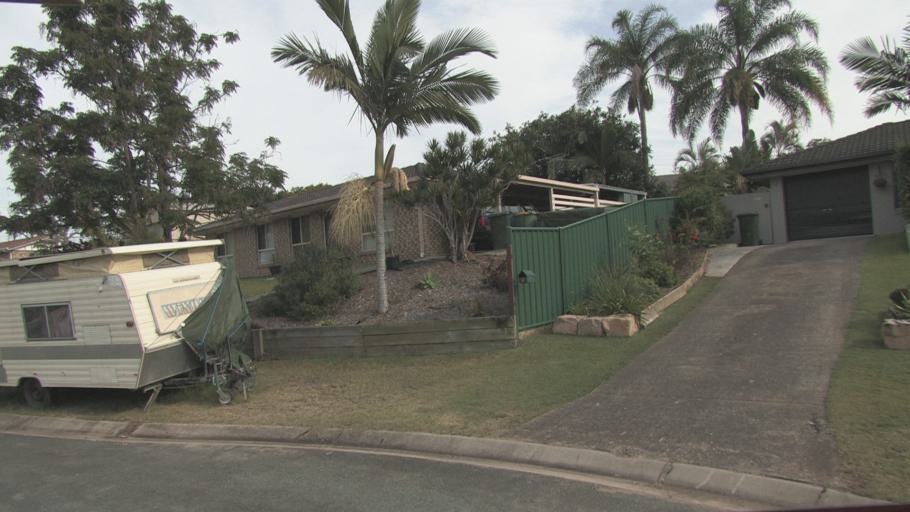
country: AU
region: Queensland
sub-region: Logan
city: Beenleigh
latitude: -27.7020
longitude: 153.1790
